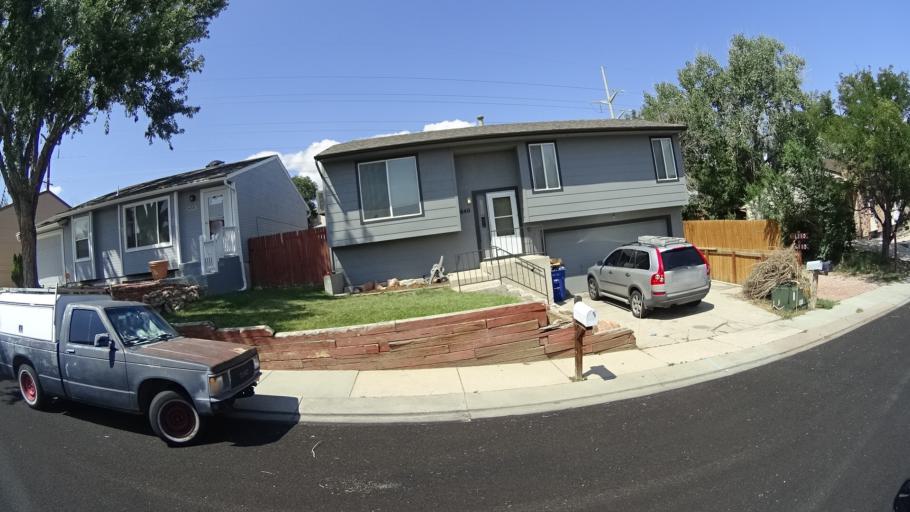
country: US
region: Colorado
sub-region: El Paso County
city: Colorado Springs
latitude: 38.8706
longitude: -104.8374
